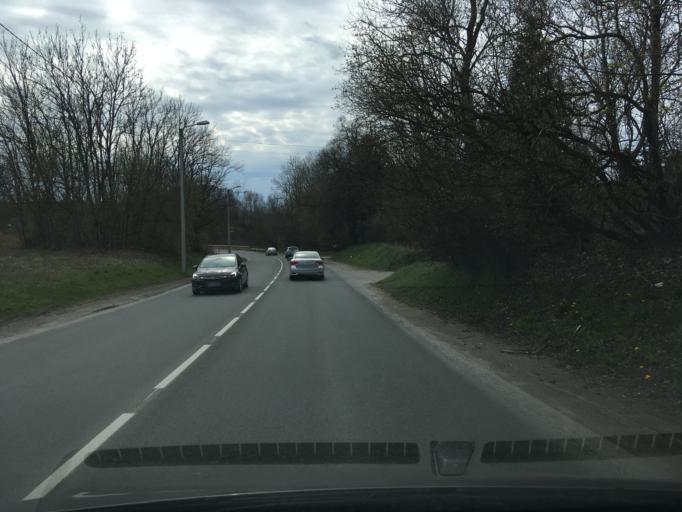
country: EE
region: Harju
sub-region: Tallinna linn
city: Kose
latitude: 59.4597
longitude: 24.9030
